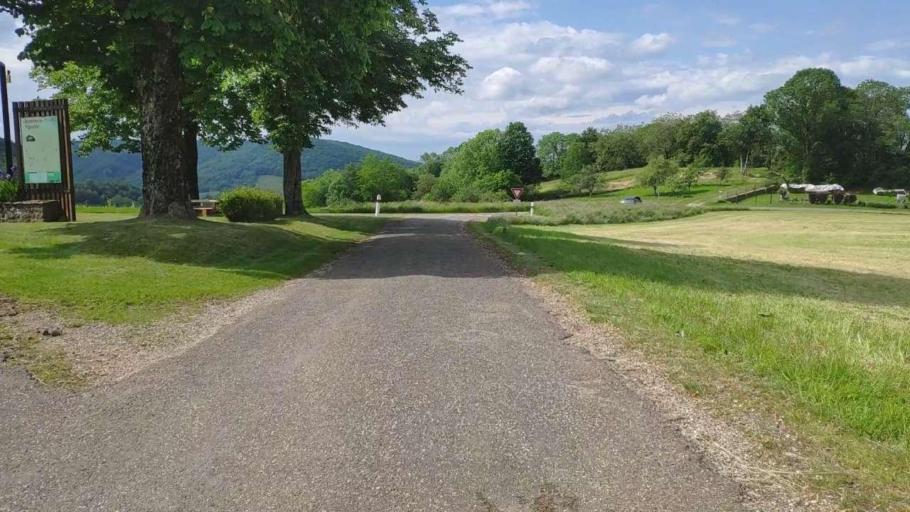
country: FR
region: Franche-Comte
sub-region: Departement du Jura
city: Perrigny
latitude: 46.7665
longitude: 5.6198
